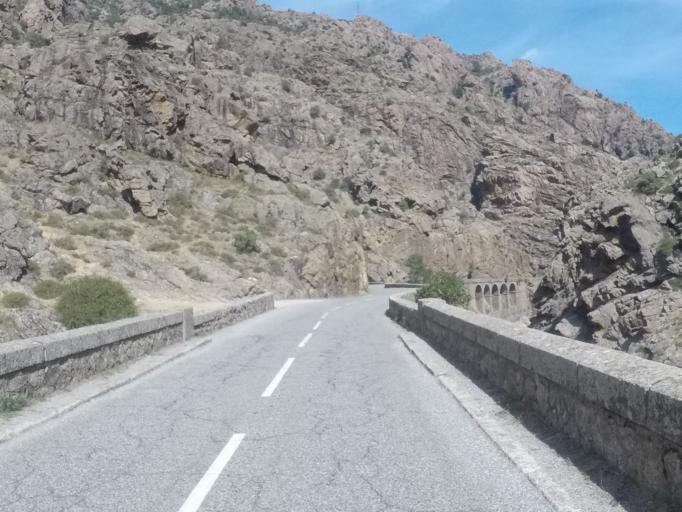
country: FR
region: Corsica
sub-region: Departement de la Haute-Corse
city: Corte
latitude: 42.3660
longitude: 9.0686
